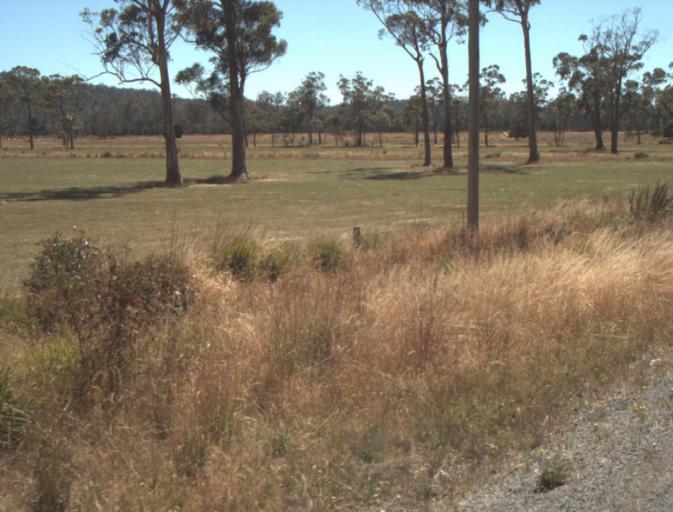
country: AU
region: Tasmania
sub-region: Launceston
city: Newstead
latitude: -41.3651
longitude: 147.3317
